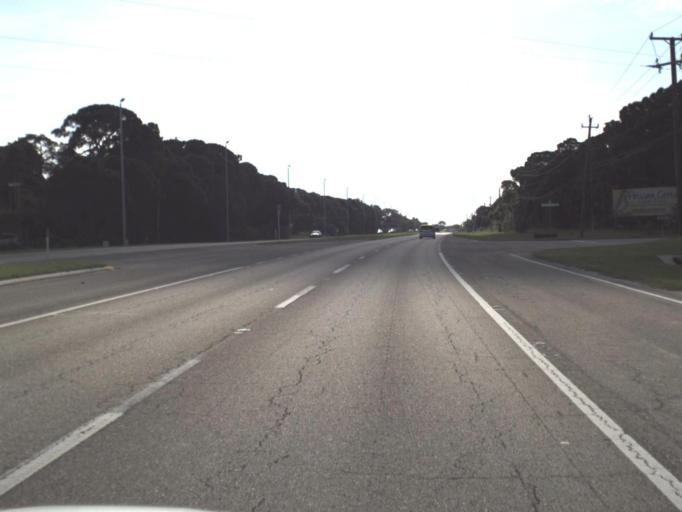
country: US
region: Florida
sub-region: Sarasota County
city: Gulf Gate Estates
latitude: 27.2408
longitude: -82.5062
